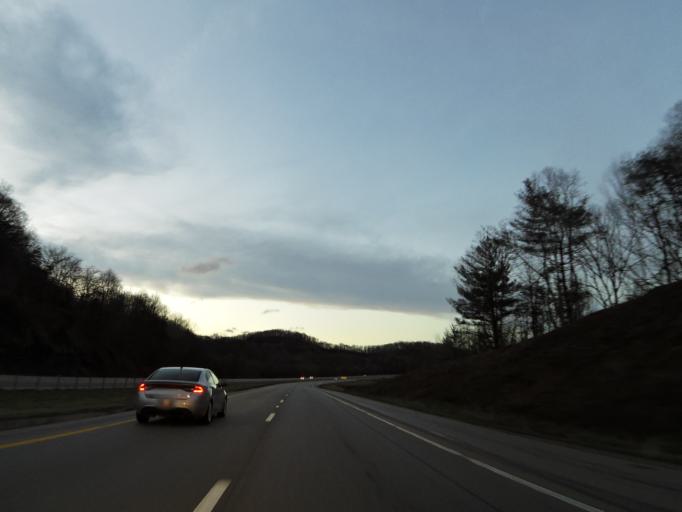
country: US
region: Tennessee
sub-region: Campbell County
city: Jellico
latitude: 36.6274
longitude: -84.1123
